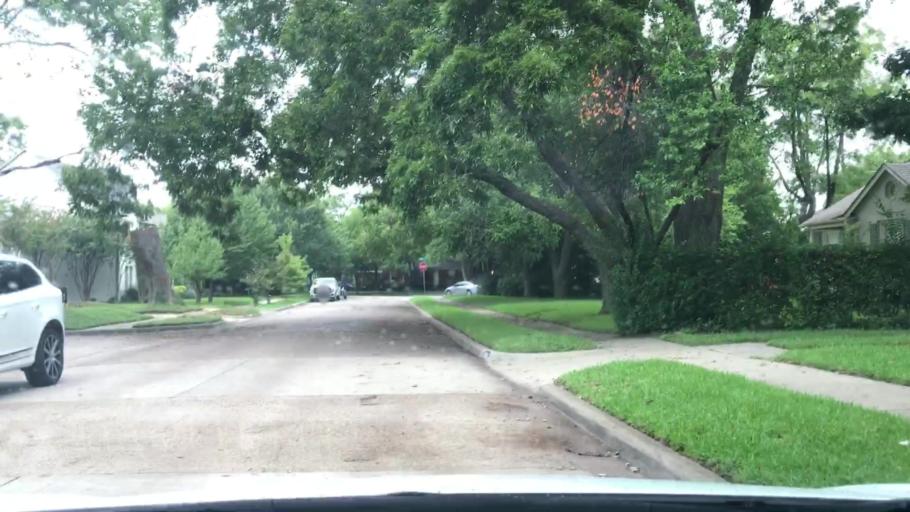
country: US
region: Texas
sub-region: Dallas County
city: University Park
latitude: 32.8543
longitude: -96.8294
